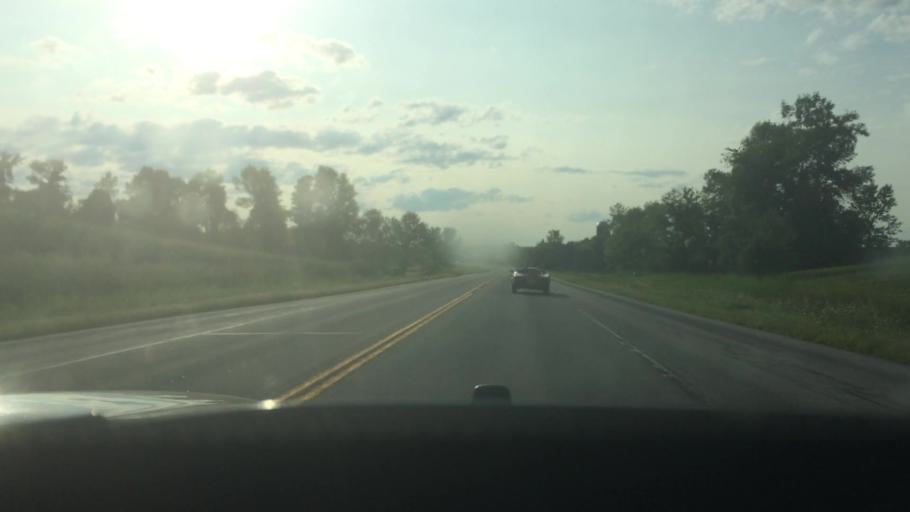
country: US
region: New York
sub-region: St. Lawrence County
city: Canton
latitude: 44.6343
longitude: -75.2562
